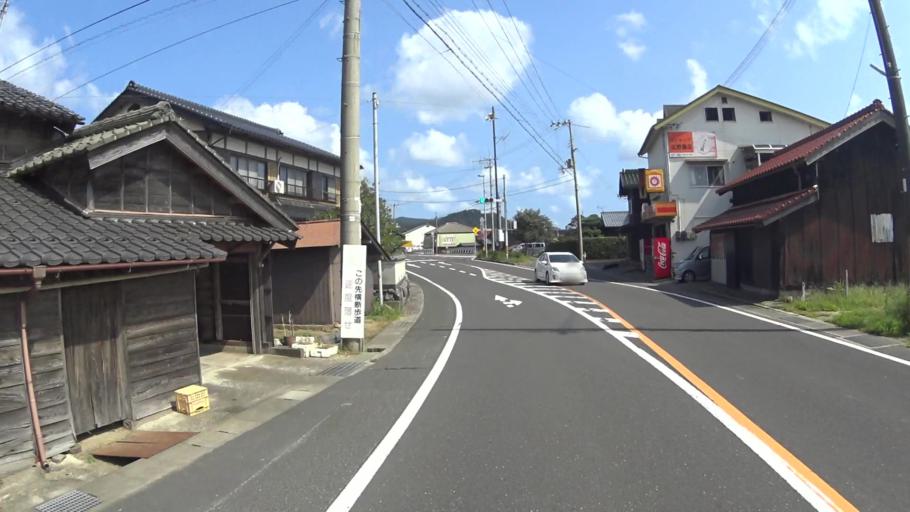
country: JP
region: Kyoto
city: Miyazu
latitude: 35.6556
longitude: 135.2585
